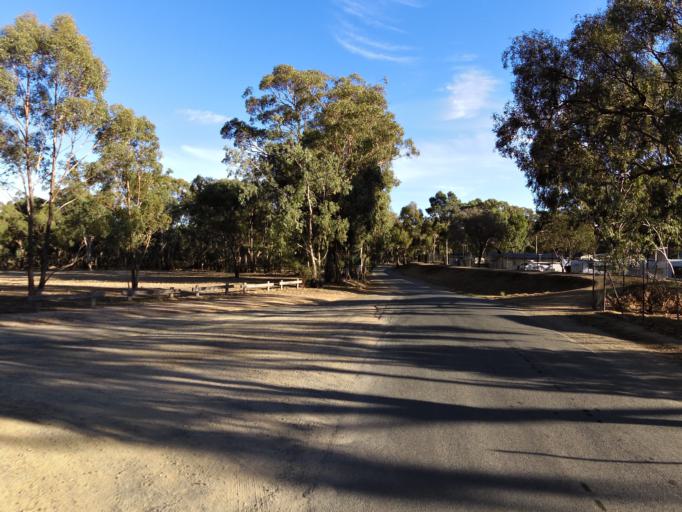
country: AU
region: New South Wales
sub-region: Murray Shire
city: Moama
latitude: -36.1155
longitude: 144.7413
